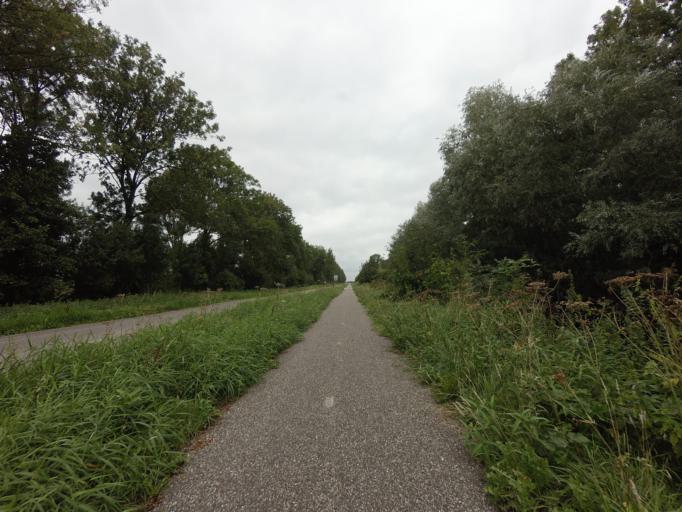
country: NL
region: Utrecht
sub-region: Gemeente De Ronde Venen
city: Mijdrecht
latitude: 52.1892
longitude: 4.9197
